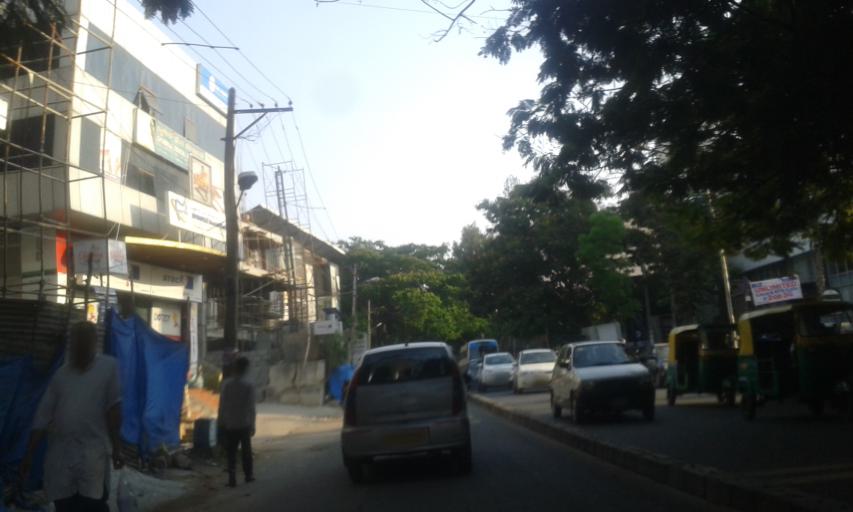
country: IN
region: Karnataka
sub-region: Bangalore Urban
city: Bangalore
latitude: 12.9538
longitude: 77.5800
